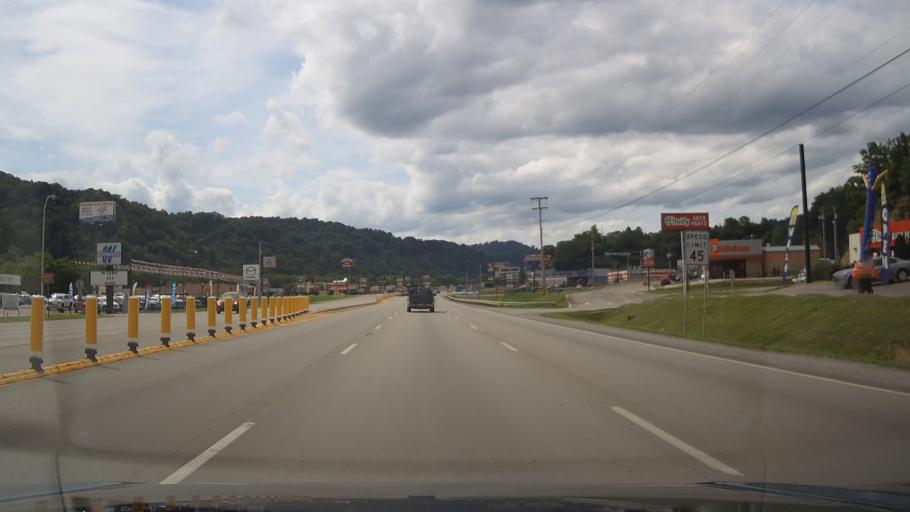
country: US
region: Kentucky
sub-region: Pike County
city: Coal Run Village
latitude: 37.5205
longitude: -82.5681
